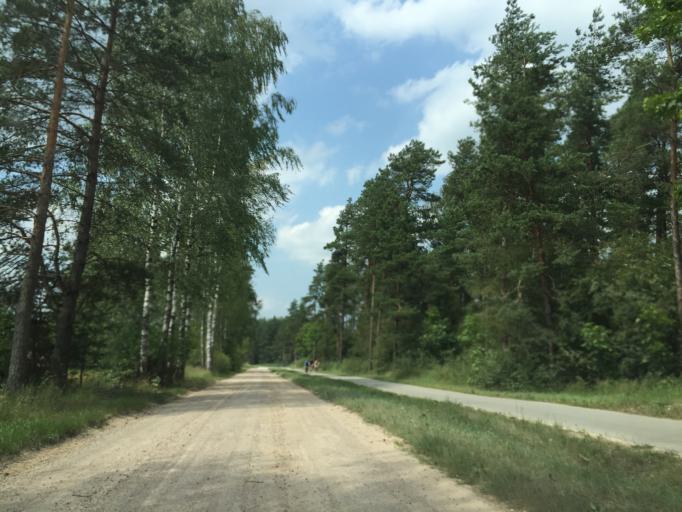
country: LV
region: Olaine
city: Olaine
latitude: 56.7775
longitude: 23.9014
